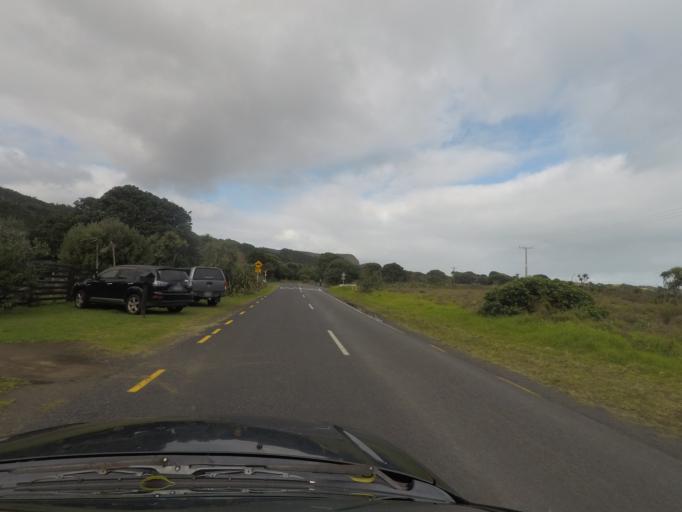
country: NZ
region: Auckland
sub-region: Auckland
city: Muriwai Beach
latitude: -36.8879
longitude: 174.4503
